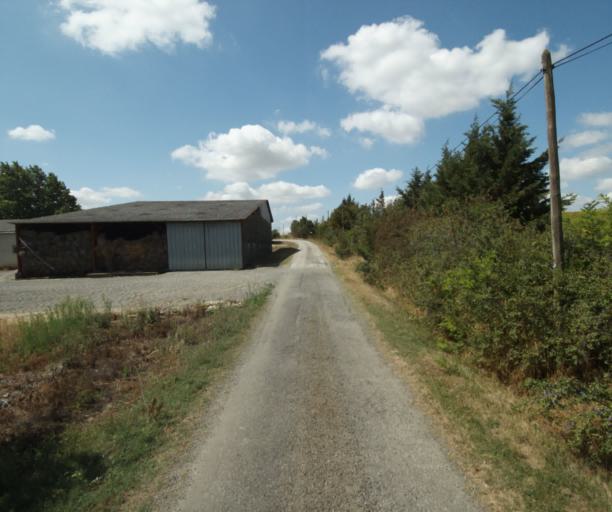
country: FR
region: Midi-Pyrenees
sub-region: Departement de la Haute-Garonne
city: Auriac-sur-Vendinelle
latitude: 43.4831
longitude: 1.8404
